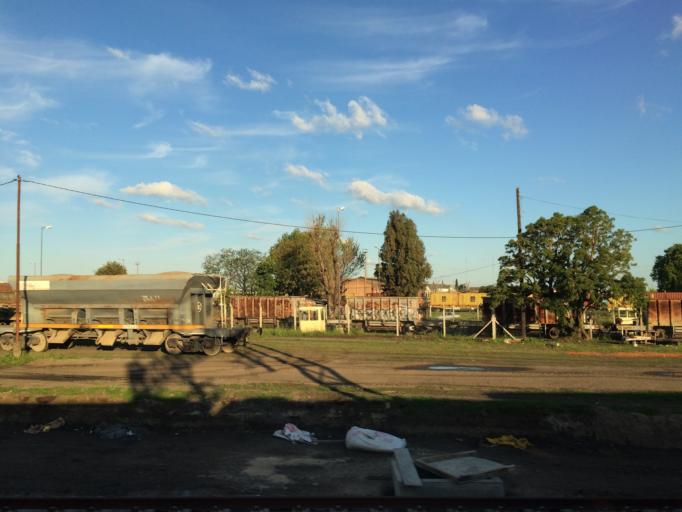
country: AR
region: Buenos Aires
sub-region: Partido de Avellaneda
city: Avellaneda
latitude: -34.6765
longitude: -58.3791
